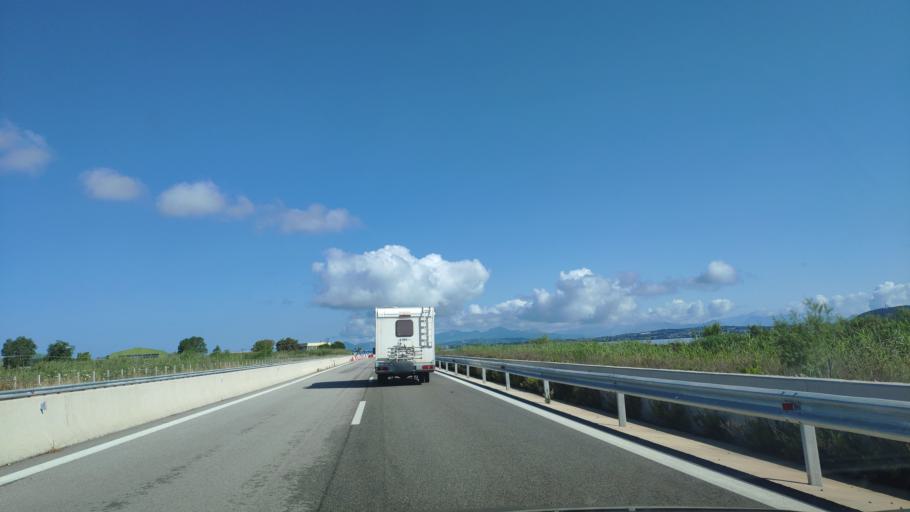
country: GR
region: Epirus
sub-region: Nomos Prevezis
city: Preveza
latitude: 38.9239
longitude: 20.7865
